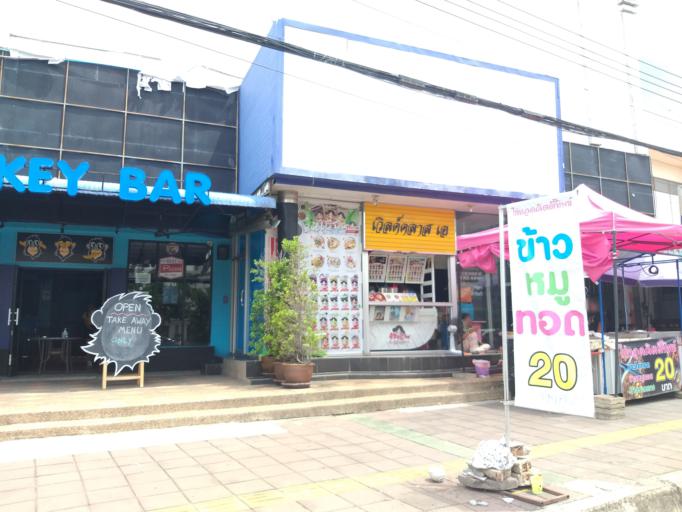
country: TH
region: Nakhon Ratchasima
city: Nakhon Ratchasima
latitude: 14.9756
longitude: 102.0874
